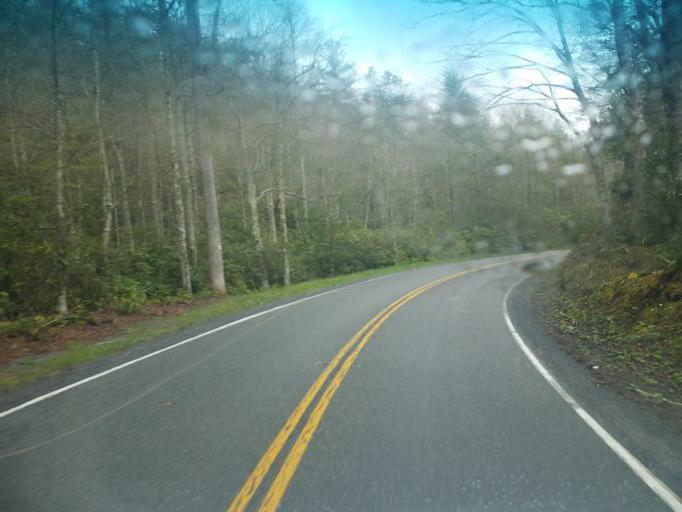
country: US
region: Virginia
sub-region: Smyth County
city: Chilhowie
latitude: 36.6459
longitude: -81.7096
